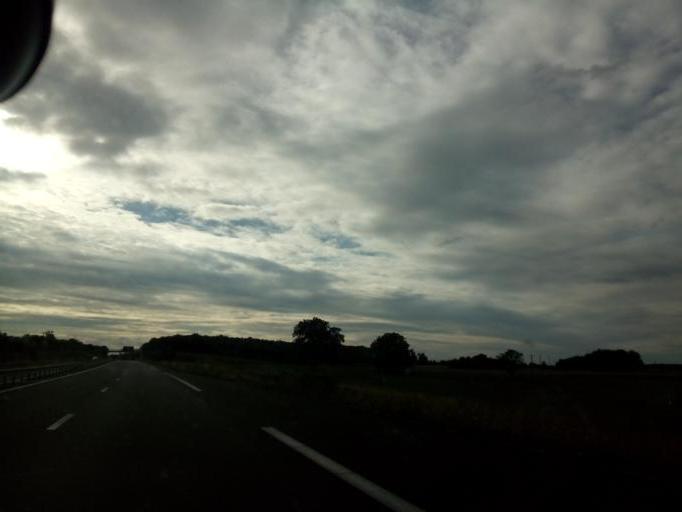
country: FR
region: Centre
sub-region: Departement d'Indre-et-Loire
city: Esvres
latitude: 47.3119
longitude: 0.7776
